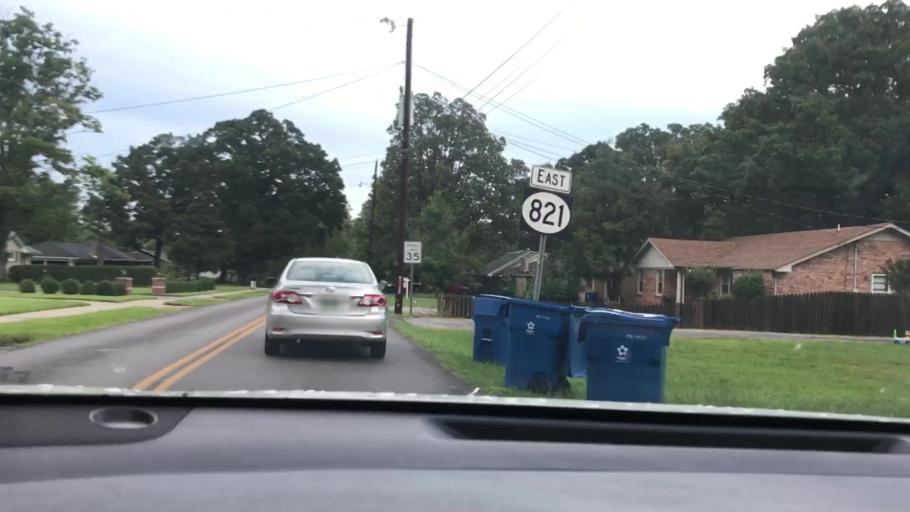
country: US
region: Kentucky
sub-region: Calloway County
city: Murray
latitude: 36.6030
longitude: -88.3243
